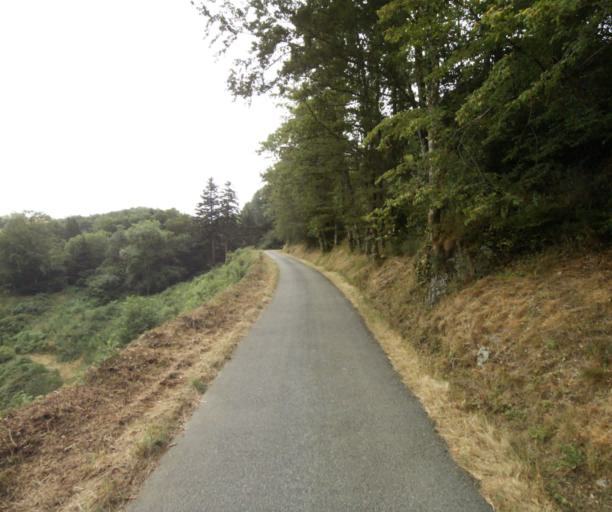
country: FR
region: Midi-Pyrenees
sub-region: Departement du Tarn
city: Soreze
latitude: 43.4166
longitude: 2.0867
